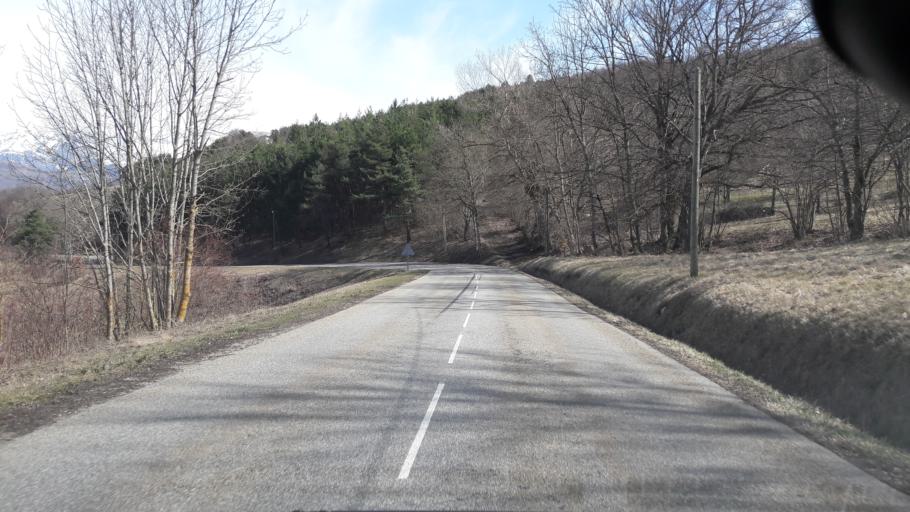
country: FR
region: Rhone-Alpes
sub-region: Departement de l'Isere
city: Mens
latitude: 44.8387
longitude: 5.7971
